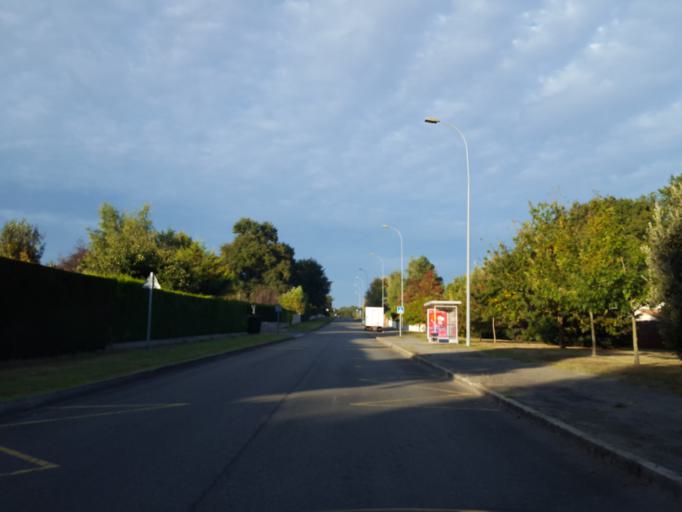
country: FR
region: Pays de la Loire
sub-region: Departement de la Loire-Atlantique
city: Haute-Goulaine
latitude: 47.2032
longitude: -1.4341
